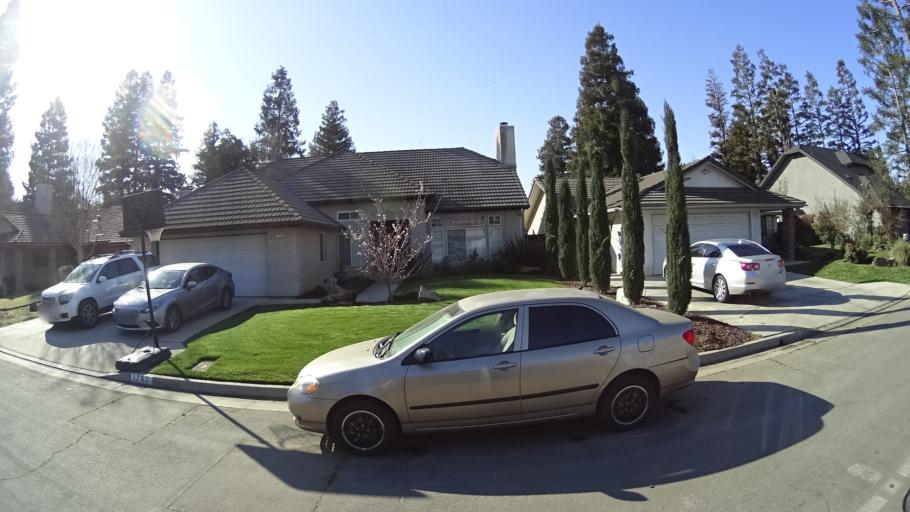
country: US
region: California
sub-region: Fresno County
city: Clovis
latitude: 36.8727
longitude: -119.7514
